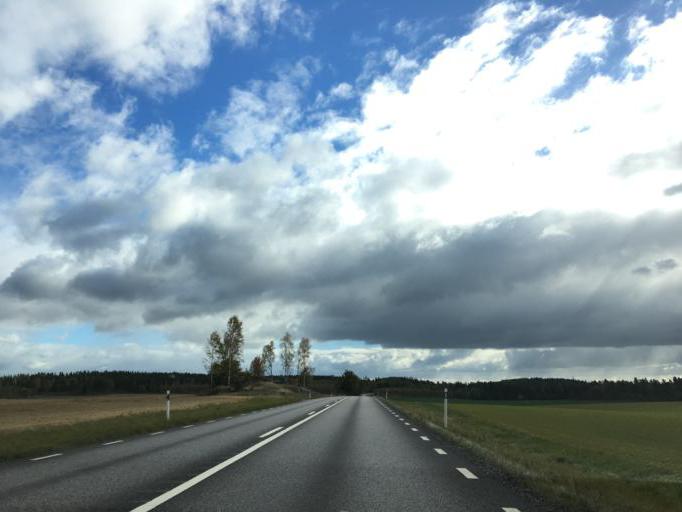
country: SE
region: Soedermanland
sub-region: Katrineholms Kommun
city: Katrineholm
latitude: 58.9414
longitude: 16.3936
